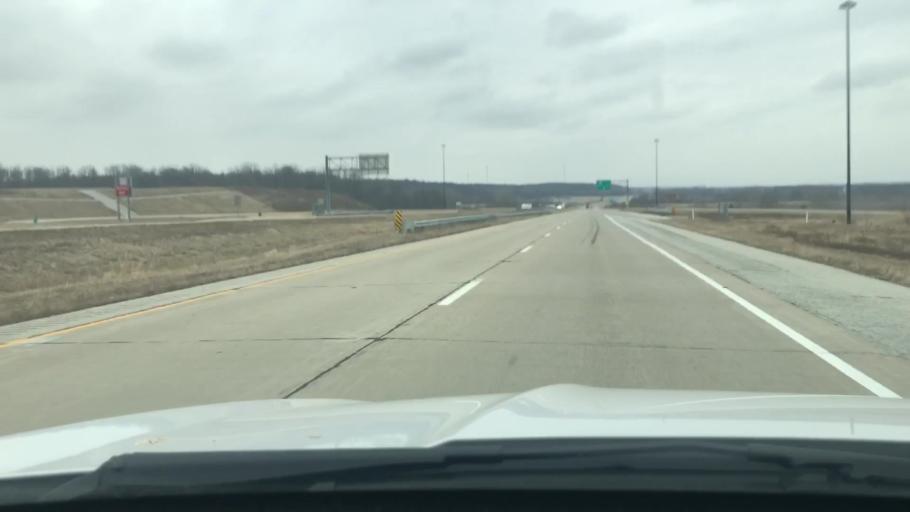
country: US
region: Indiana
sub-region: Miami County
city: Peru
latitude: 40.7718
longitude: -86.1306
